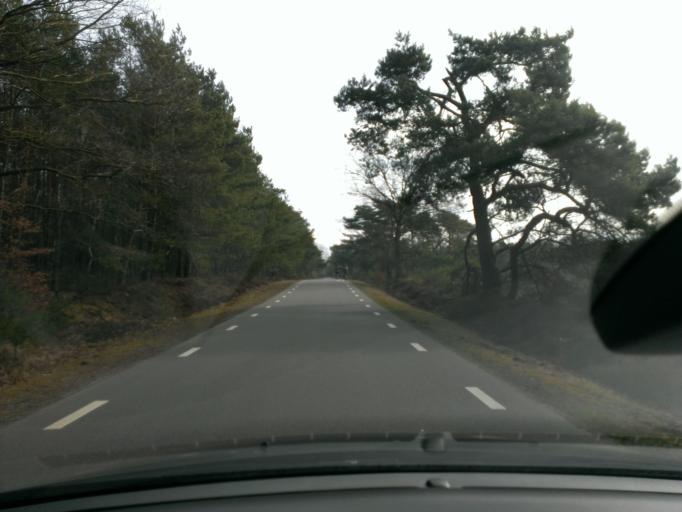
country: NL
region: Gelderland
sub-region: Gemeente Epe
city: Epe
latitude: 52.3911
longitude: 5.9918
